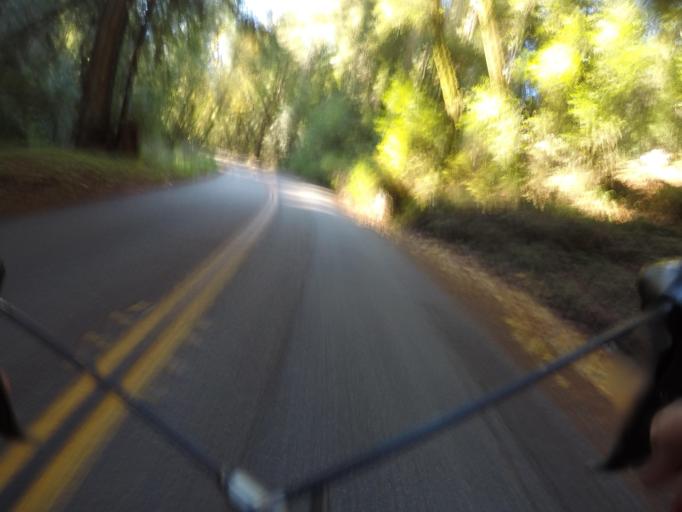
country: US
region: California
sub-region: Santa Cruz County
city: Scotts Valley
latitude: 37.0979
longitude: -121.9974
